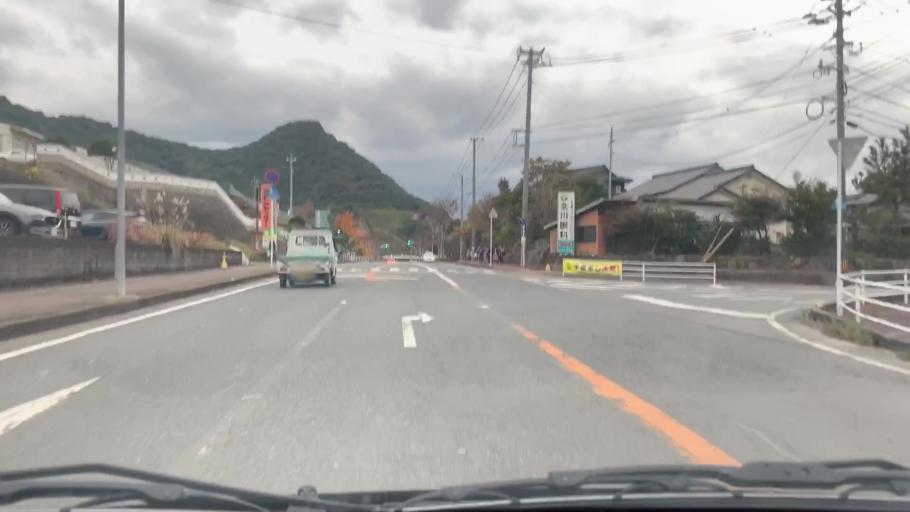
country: JP
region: Saga Prefecture
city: Takeocho-takeo
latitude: 33.1873
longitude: 130.0280
